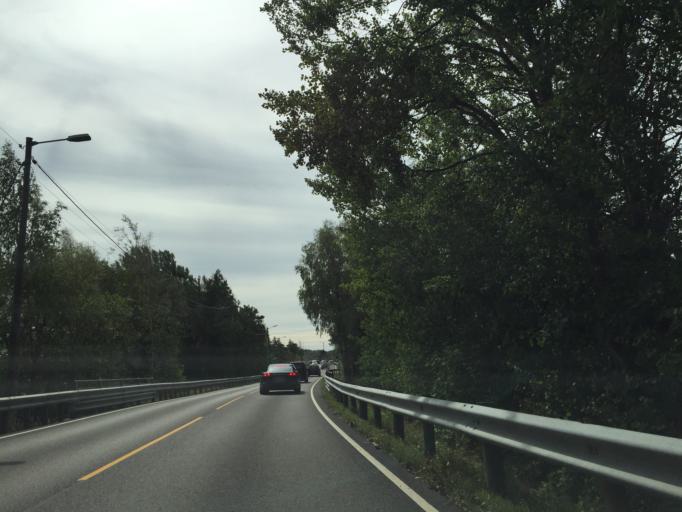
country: NO
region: Ostfold
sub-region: Fredrikstad
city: Fredrikstad
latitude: 59.1503
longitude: 10.9406
